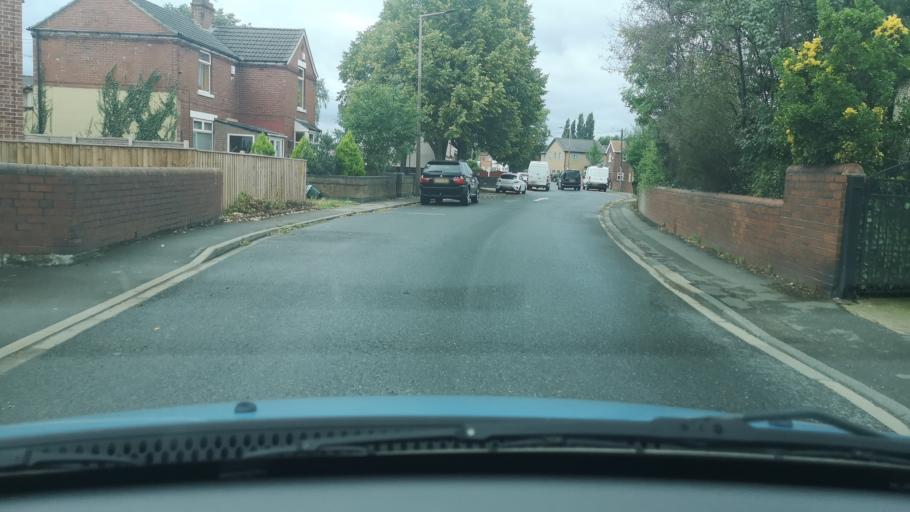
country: GB
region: England
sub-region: Doncaster
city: Stainforth
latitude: 53.5999
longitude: -1.0290
